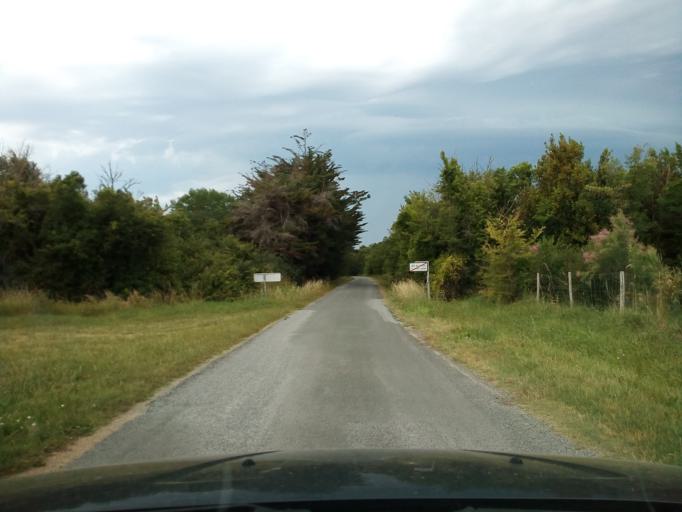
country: FR
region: Poitou-Charentes
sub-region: Departement de la Charente-Maritime
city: Dolus-d'Oleron
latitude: 45.9306
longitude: -1.2607
